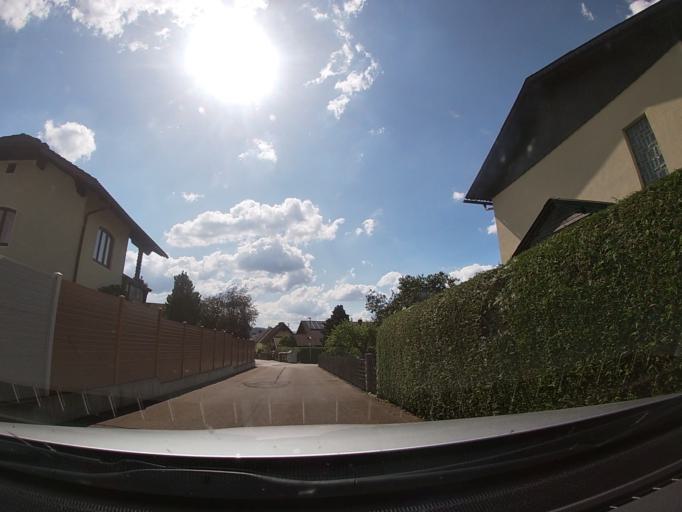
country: AT
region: Styria
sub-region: Politischer Bezirk Leoben
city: Trofaiach
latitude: 47.4246
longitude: 14.9862
